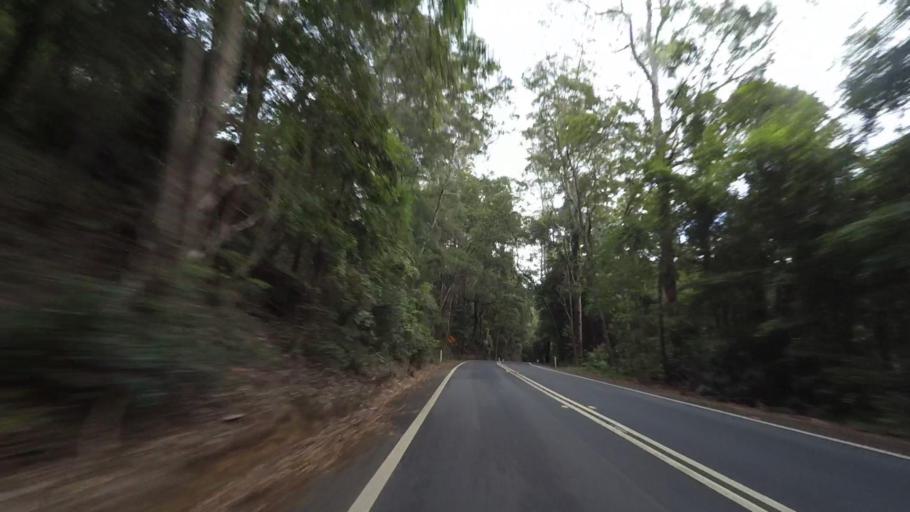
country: AU
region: New South Wales
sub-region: Wollongong
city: Helensburgh
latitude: -34.1672
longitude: 151.0167
